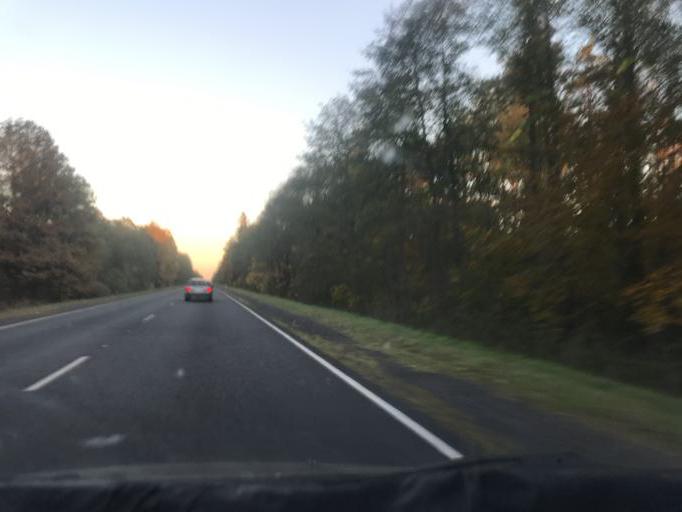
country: BY
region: Gomel
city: Mazyr
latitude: 52.1761
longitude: 29.1829
